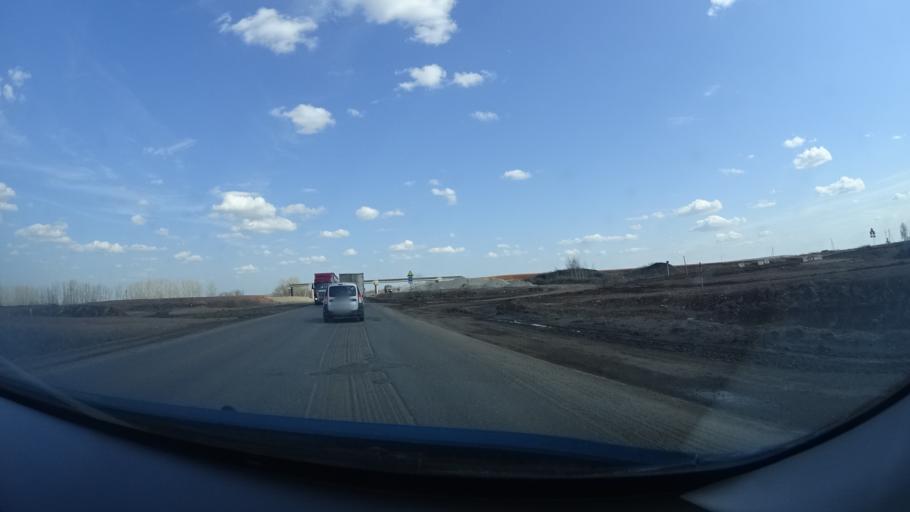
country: RU
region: Bashkortostan
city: Buzdyak
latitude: 54.6498
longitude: 54.5994
